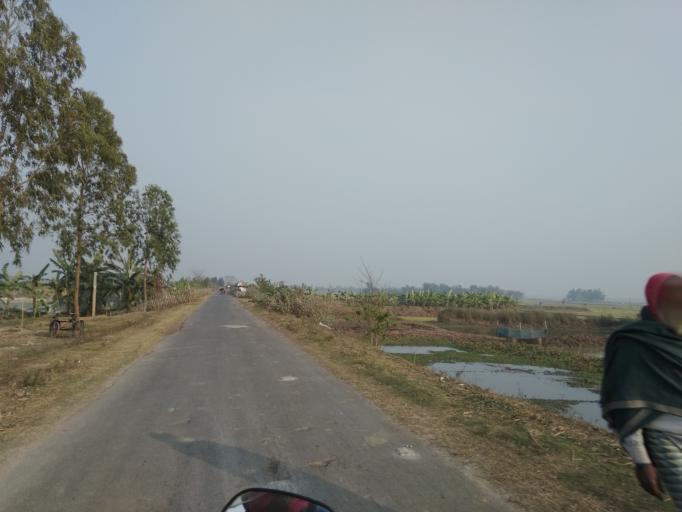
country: BD
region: Rajshahi
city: Par Naogaon
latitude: 24.4987
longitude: 89.1577
